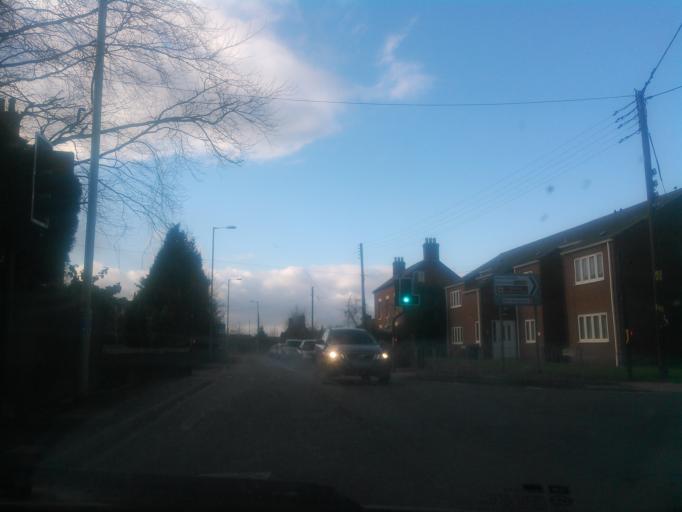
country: GB
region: England
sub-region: Shropshire
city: Shawbury
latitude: 52.7873
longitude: -2.6562
